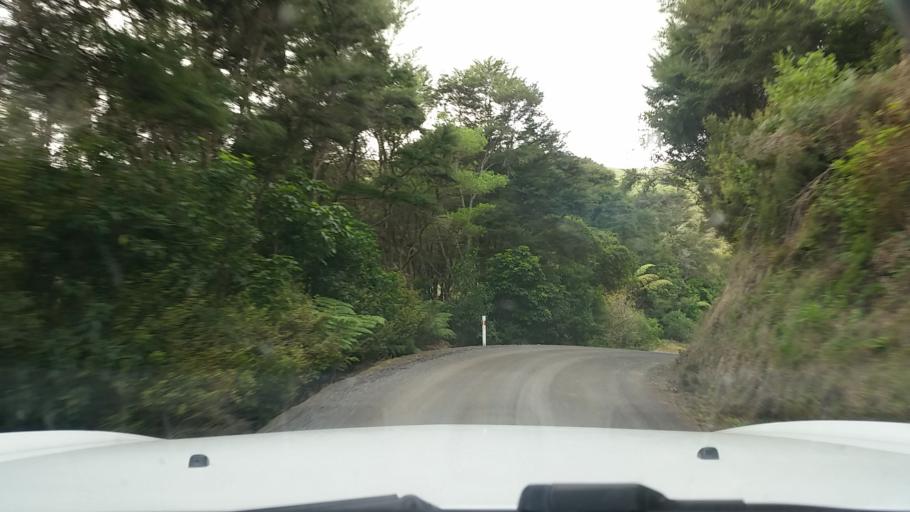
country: NZ
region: Waikato
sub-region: Hauraki District
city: Ngatea
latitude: -37.4830
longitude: 175.4513
